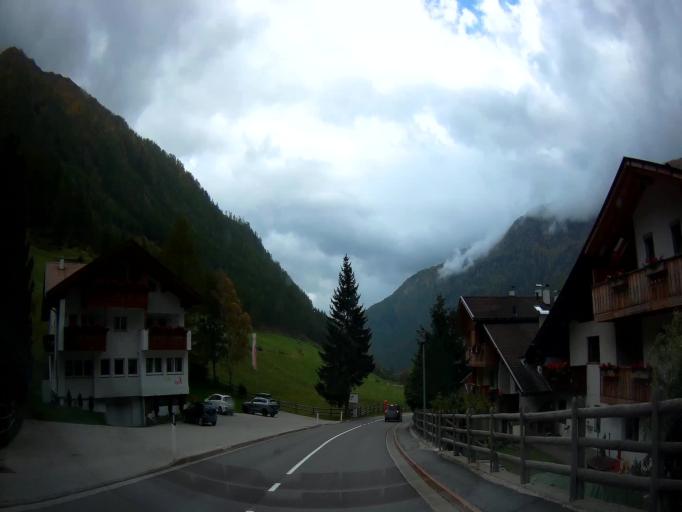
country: IT
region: Trentino-Alto Adige
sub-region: Bolzano
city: Senales
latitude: 46.7255
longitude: 10.8578
